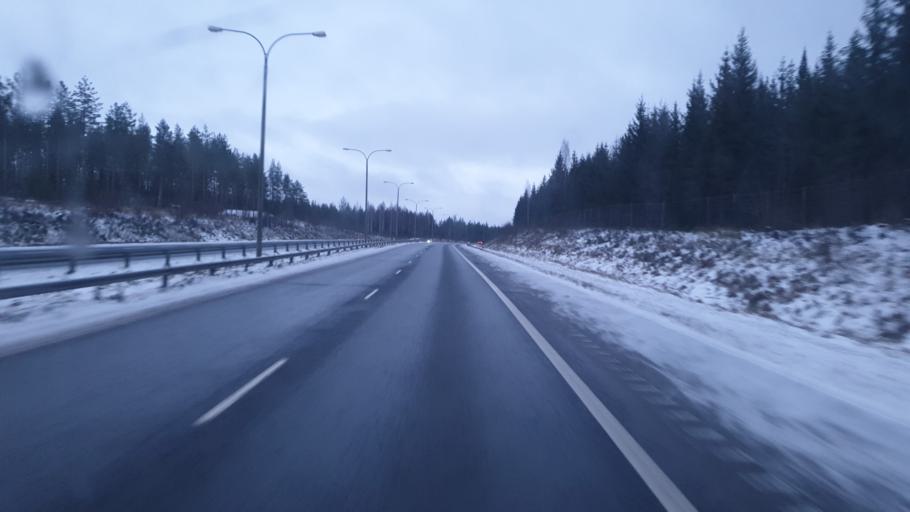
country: FI
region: Northern Savo
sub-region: Kuopio
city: Siilinjaervi
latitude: 63.0150
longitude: 27.6691
